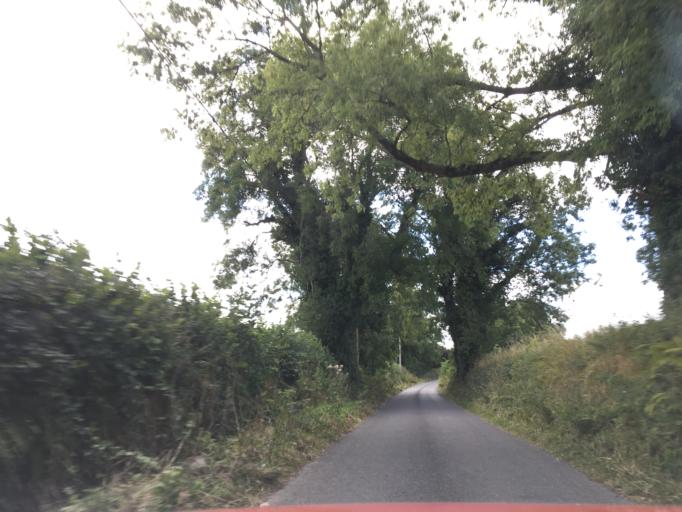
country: IE
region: Munster
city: Cashel
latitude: 52.4953
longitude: -7.9161
